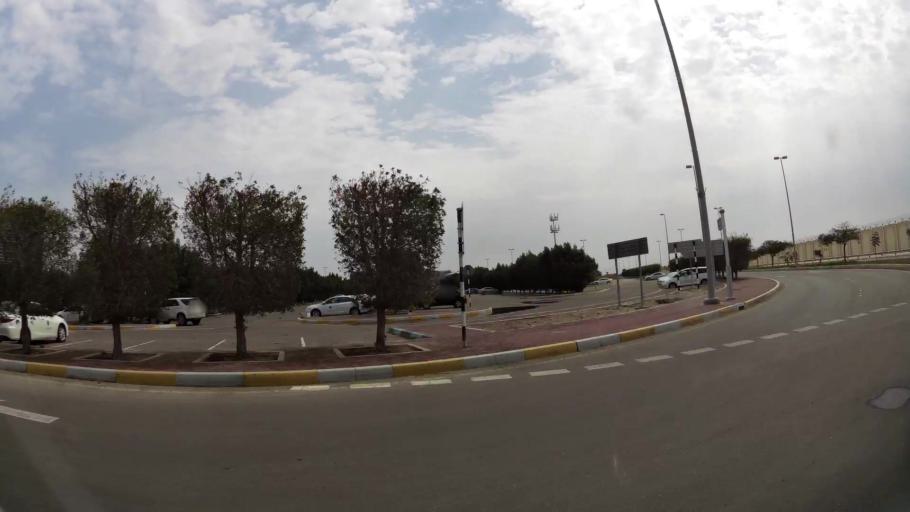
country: AE
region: Abu Dhabi
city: Abu Dhabi
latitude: 24.4272
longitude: 54.4633
